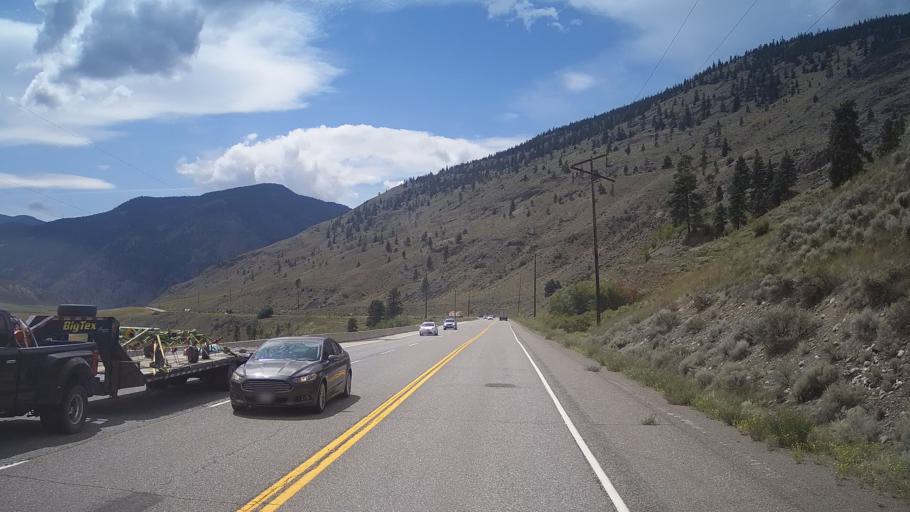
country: CA
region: British Columbia
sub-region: Thompson-Nicola Regional District
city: Ashcroft
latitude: 50.4525
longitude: -121.3089
